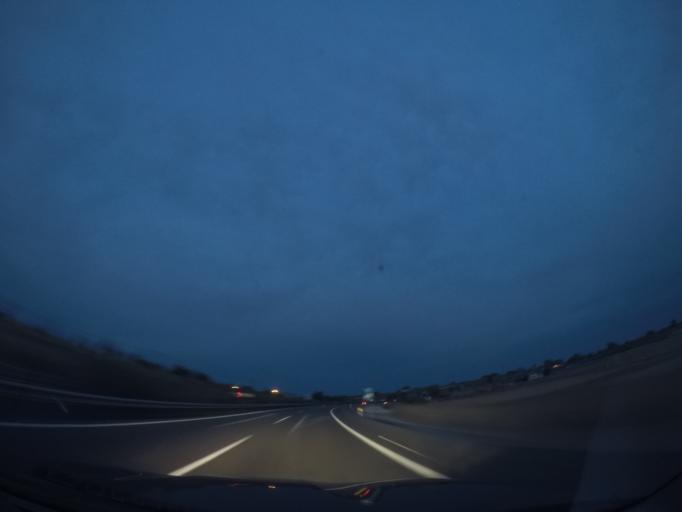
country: ES
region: Andalusia
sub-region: Provincia de Sevilla
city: La Puebla de Cazalla
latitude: 37.2348
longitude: -5.3701
